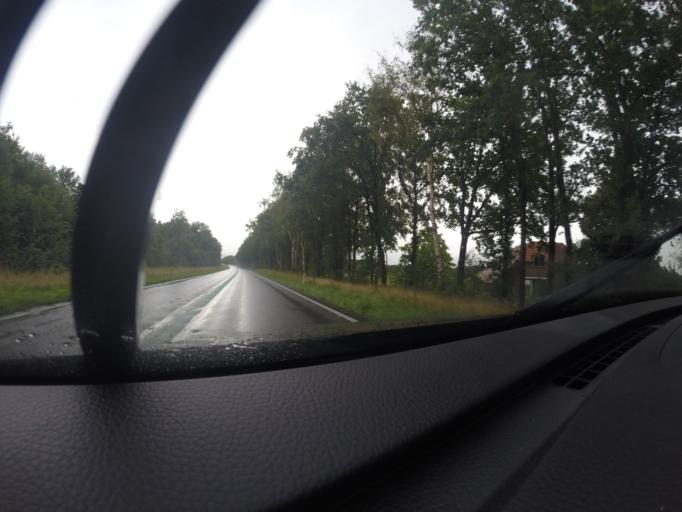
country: NL
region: Gelderland
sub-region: Gemeente Lochem
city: Laren
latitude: 52.2250
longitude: 6.3951
